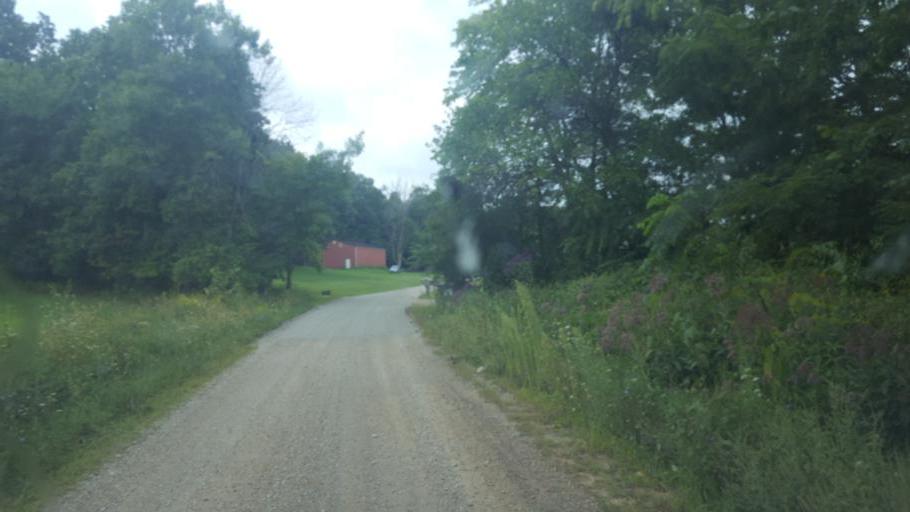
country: US
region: Ohio
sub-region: Knox County
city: Danville
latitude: 40.4760
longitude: -82.3208
